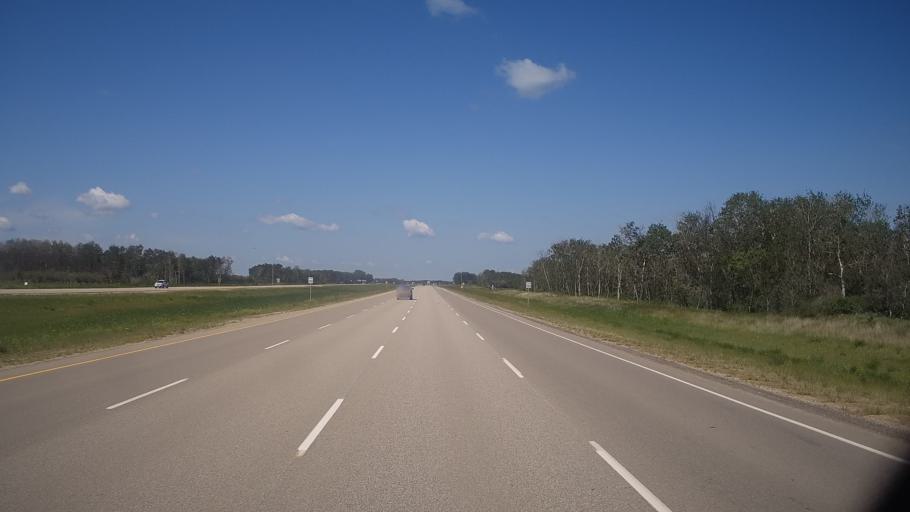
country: CA
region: Saskatchewan
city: Saskatoon
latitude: 52.0123
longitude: -106.3883
